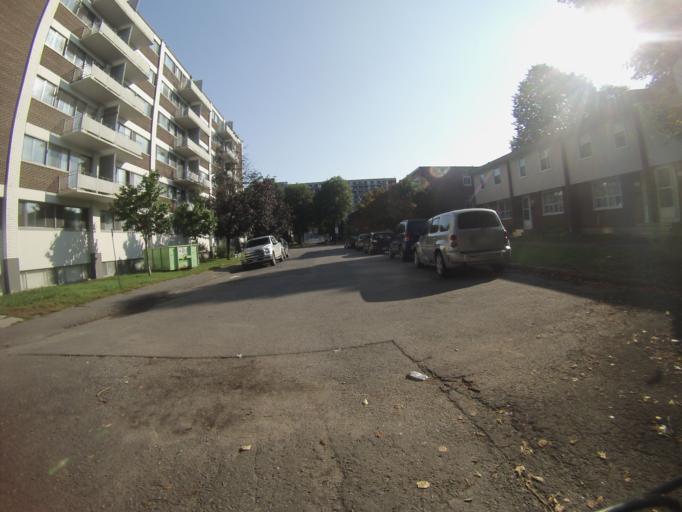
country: CA
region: Ontario
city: Ottawa
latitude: 45.4323
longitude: -75.6852
